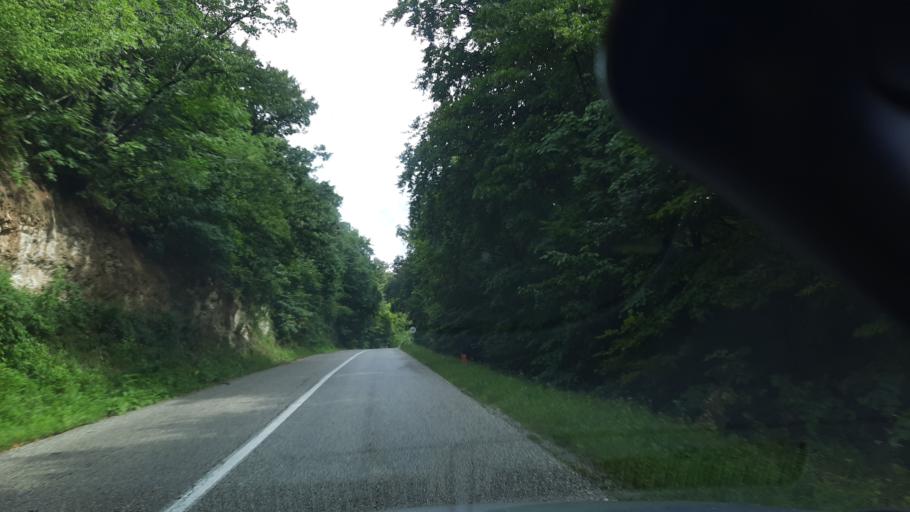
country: RS
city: Glozan
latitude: 45.1397
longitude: 19.5794
